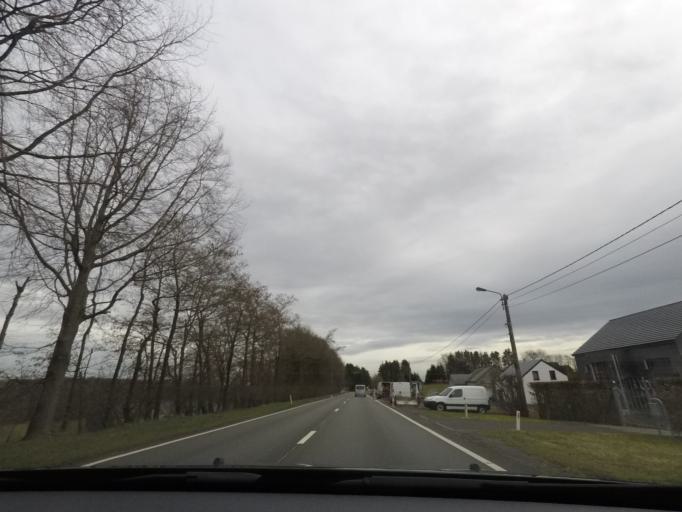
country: LU
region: Diekirch
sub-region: Canton de Wiltz
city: Winseler
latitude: 49.9851
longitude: 5.8266
